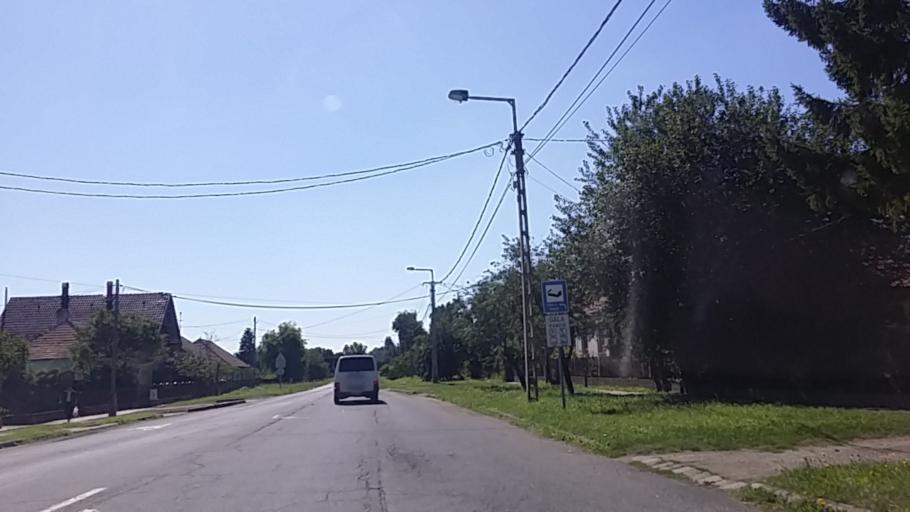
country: HU
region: Tolna
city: Simontornya
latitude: 46.7570
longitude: 18.5433
